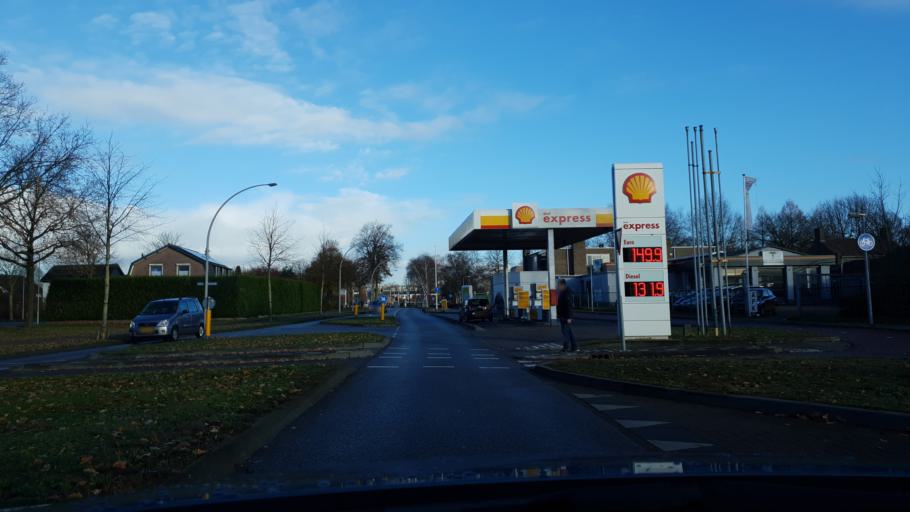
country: NL
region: Gelderland
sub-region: Gemeente Wijchen
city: Wijchen
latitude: 51.8074
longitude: 5.7202
